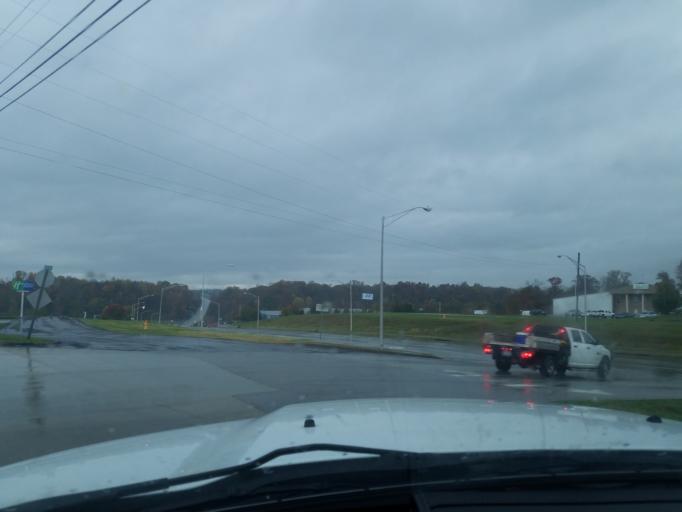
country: US
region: Kentucky
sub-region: Taylor County
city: Campbellsville
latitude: 37.3471
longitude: -85.3729
